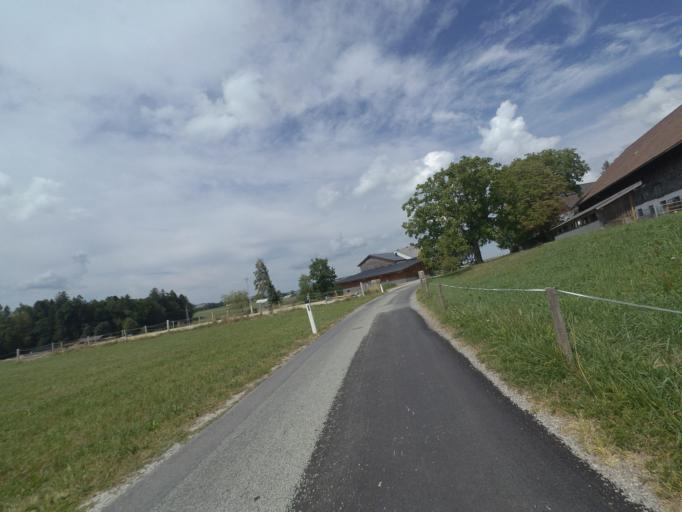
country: AT
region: Salzburg
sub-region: Politischer Bezirk Salzburg-Umgebung
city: Obertrum am See
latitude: 47.9045
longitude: 13.0927
